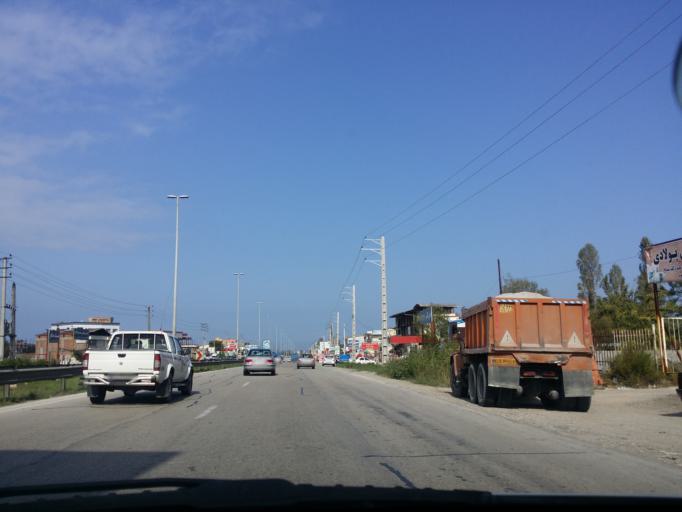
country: IR
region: Mazandaran
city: Chalus
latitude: 36.6608
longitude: 51.3996
